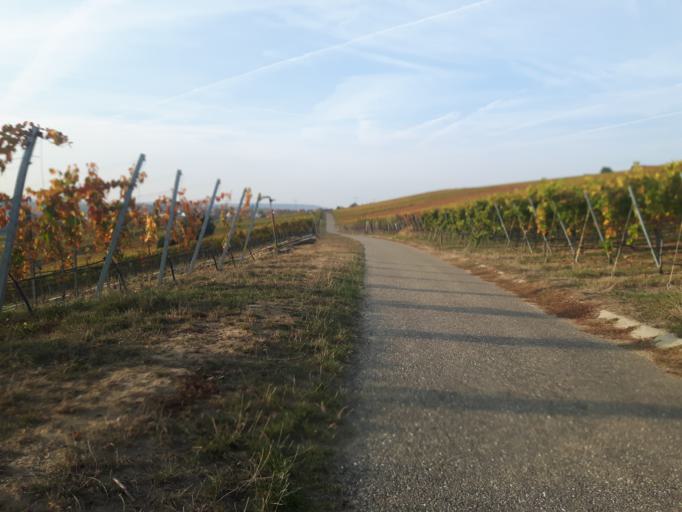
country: DE
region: Baden-Wuerttemberg
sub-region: Regierungsbezirk Stuttgart
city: Talheim
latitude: 49.0686
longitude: 9.1761
